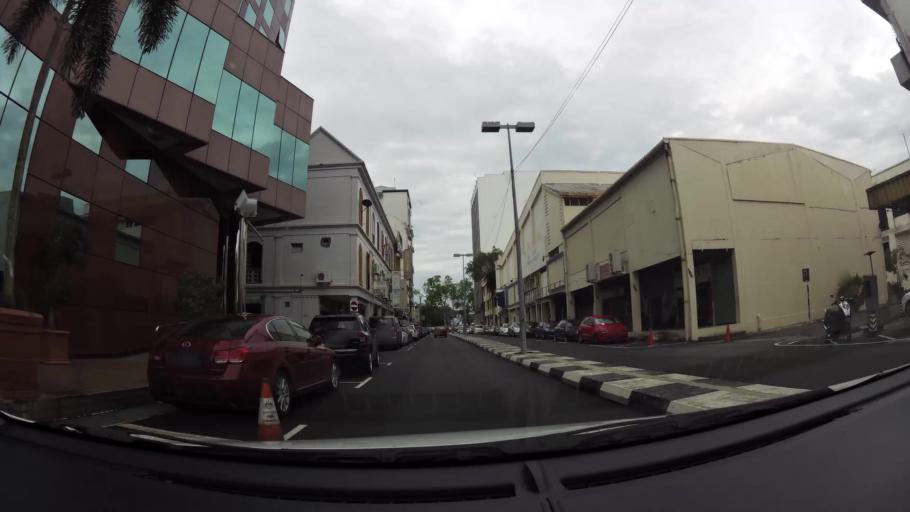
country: BN
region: Brunei and Muara
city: Bandar Seri Begawan
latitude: 4.8885
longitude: 114.9419
